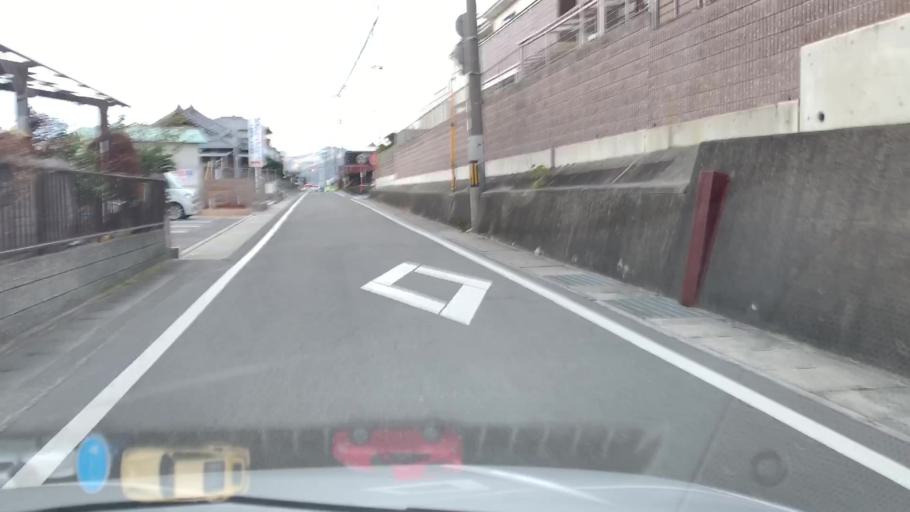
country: JP
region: Wakayama
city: Iwade
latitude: 34.2654
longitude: 135.2954
